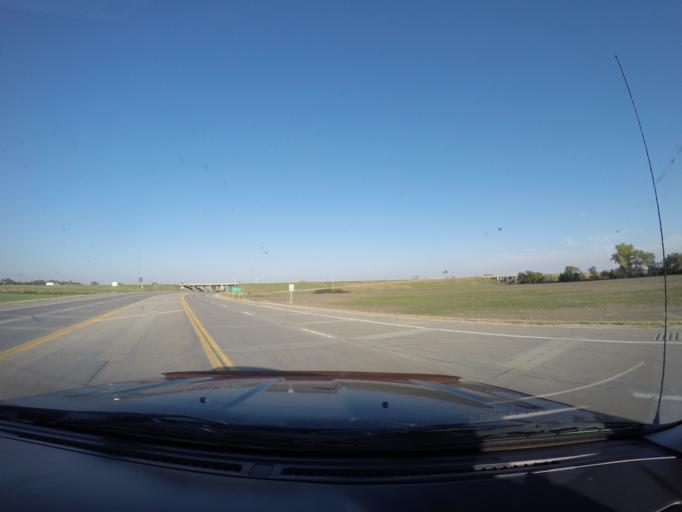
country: US
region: Kansas
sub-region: Saline County
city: Salina
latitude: 38.8401
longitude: -97.6491
